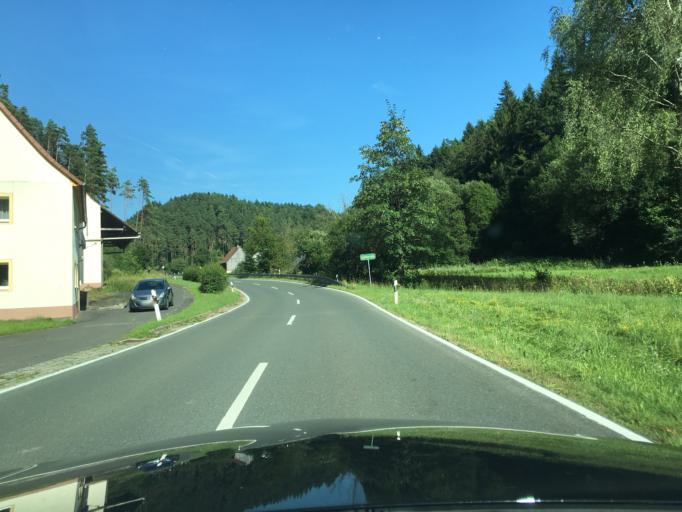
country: DE
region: Bavaria
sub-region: Upper Franconia
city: Obertrubach
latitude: 49.6903
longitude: 11.3361
